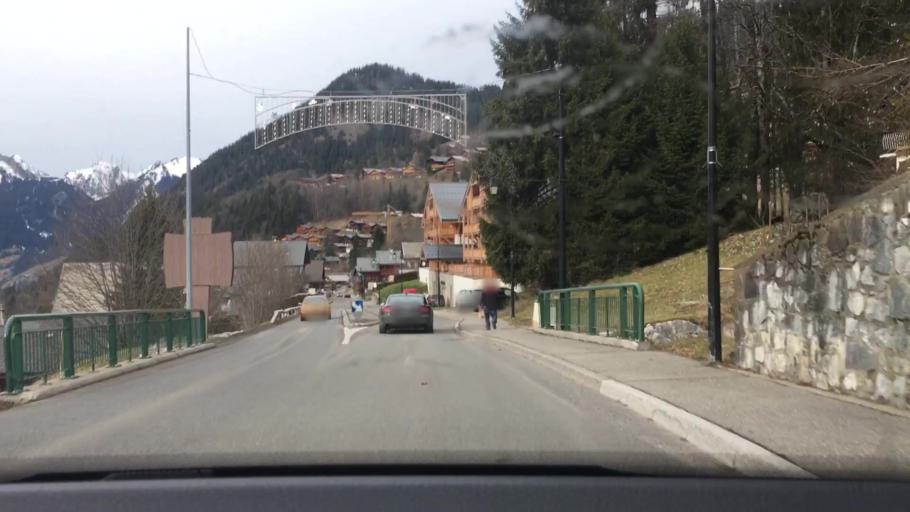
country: FR
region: Rhone-Alpes
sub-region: Departement de la Haute-Savoie
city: Chatel
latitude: 46.2712
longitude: 6.8396
